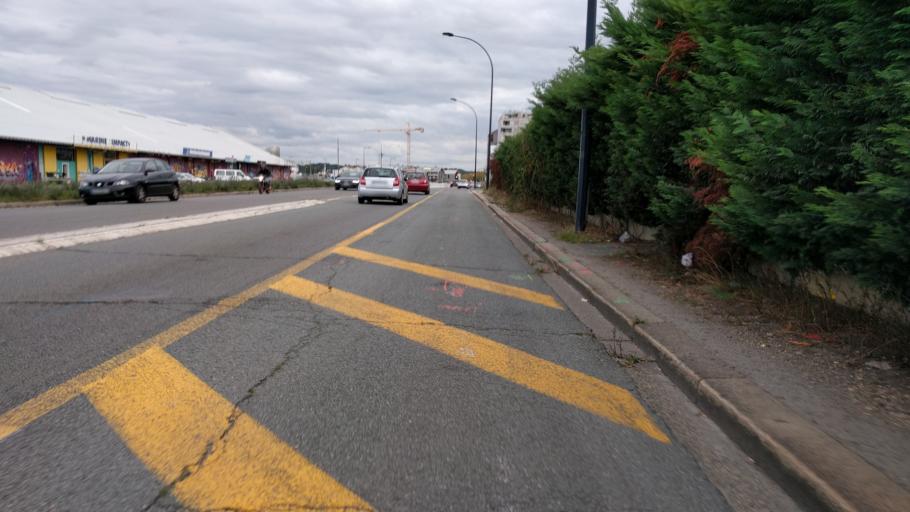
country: FR
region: Aquitaine
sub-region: Departement de la Gironde
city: Le Bouscat
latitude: 44.8674
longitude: -0.5633
